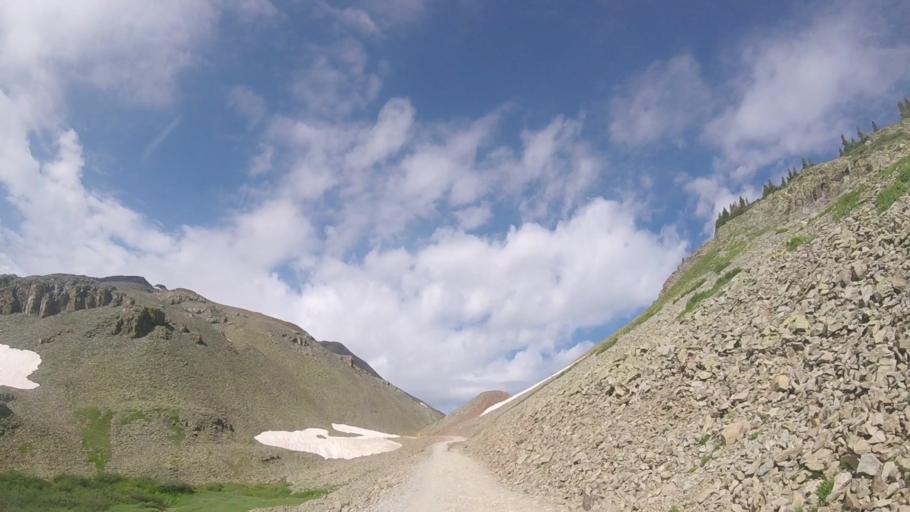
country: US
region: Colorado
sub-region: San Miguel County
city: Telluride
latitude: 37.8514
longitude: -107.7769
